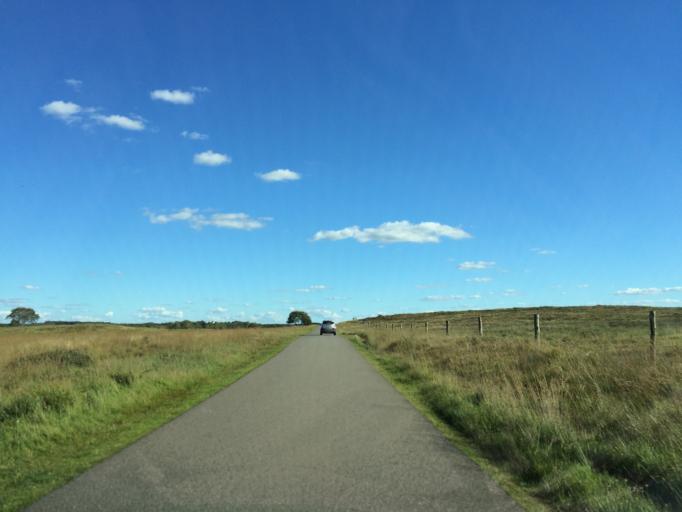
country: DK
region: Central Jutland
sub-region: Holstebro Kommune
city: Holstebro
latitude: 56.2699
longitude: 8.5161
